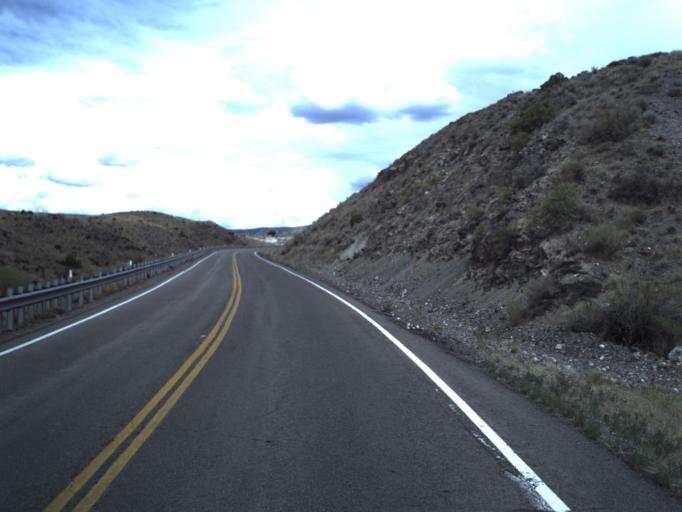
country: US
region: Utah
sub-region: Sevier County
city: Richfield
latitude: 38.7672
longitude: -111.9743
